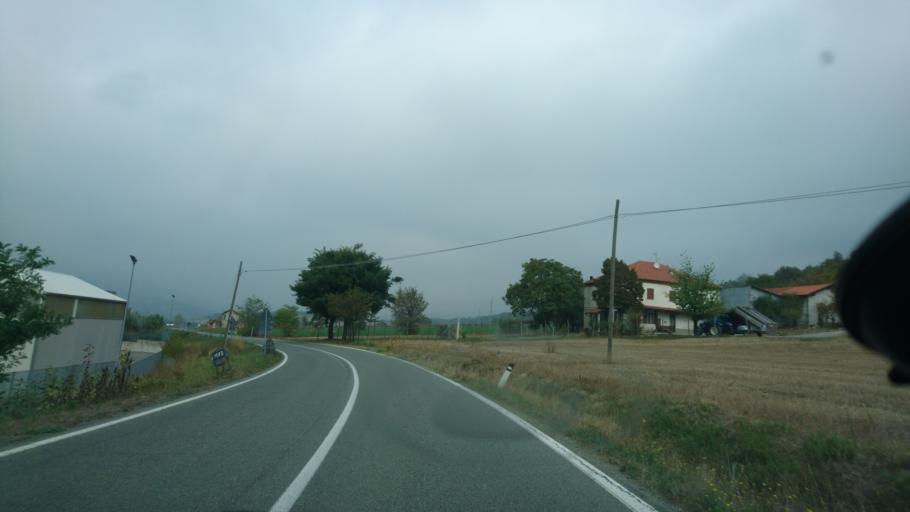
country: IT
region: Piedmont
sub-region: Provincia di Asti
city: Mombaldone
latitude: 44.5641
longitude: 8.3461
